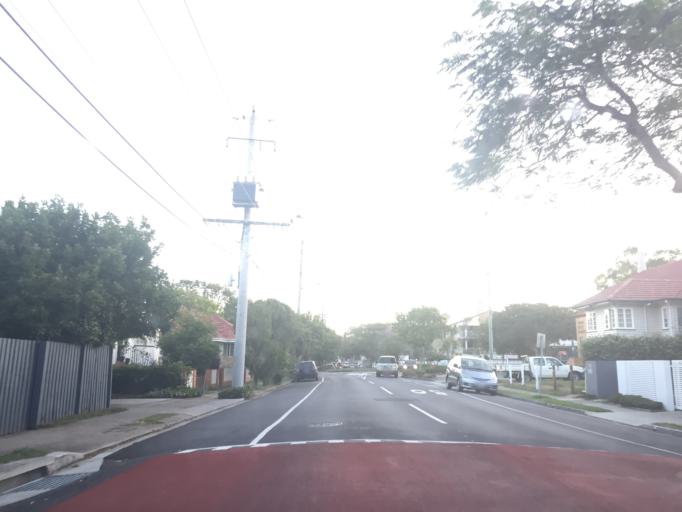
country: AU
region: Queensland
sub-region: Brisbane
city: Milton
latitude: -27.4625
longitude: 152.9968
